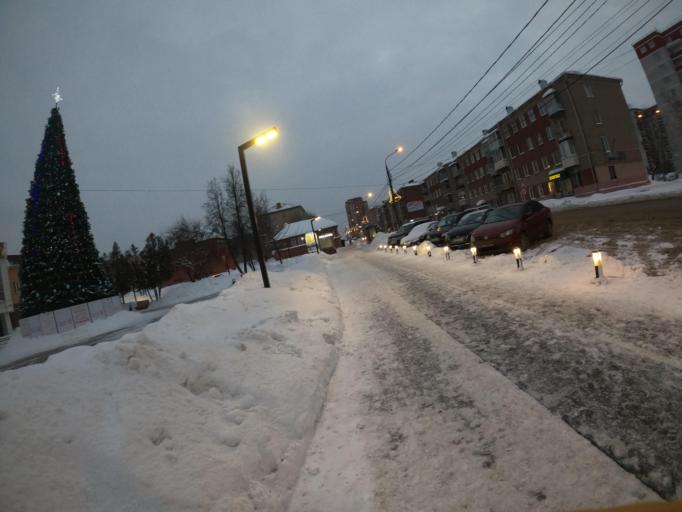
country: RU
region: Moskovskaya
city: Pavlovskiy Posad
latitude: 55.7804
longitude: 38.6711
